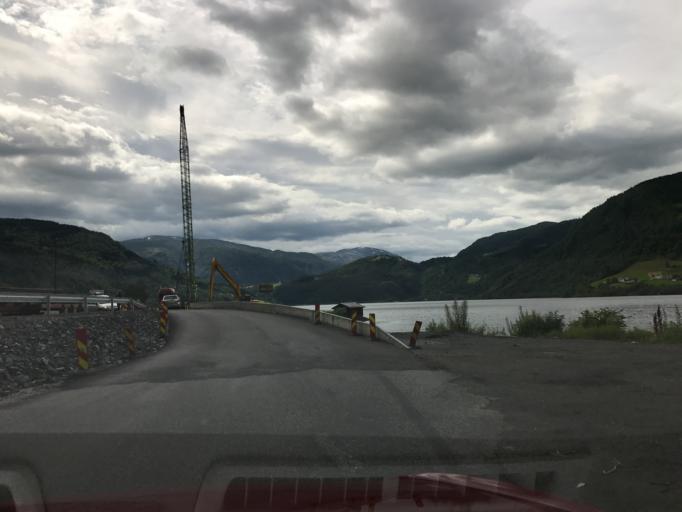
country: NO
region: Hordaland
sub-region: Granvin
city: Granvin
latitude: 60.5674
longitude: 6.7224
